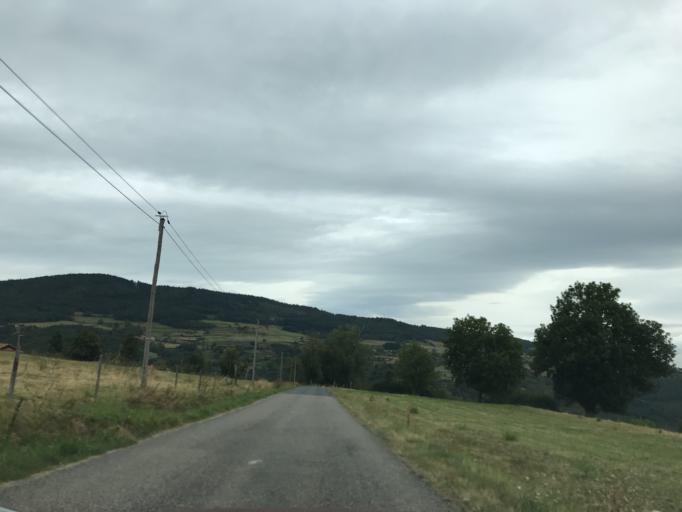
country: FR
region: Rhone-Alpes
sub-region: Departement de la Loire
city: Sail-sous-Couzan
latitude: 45.6767
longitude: 3.9069
